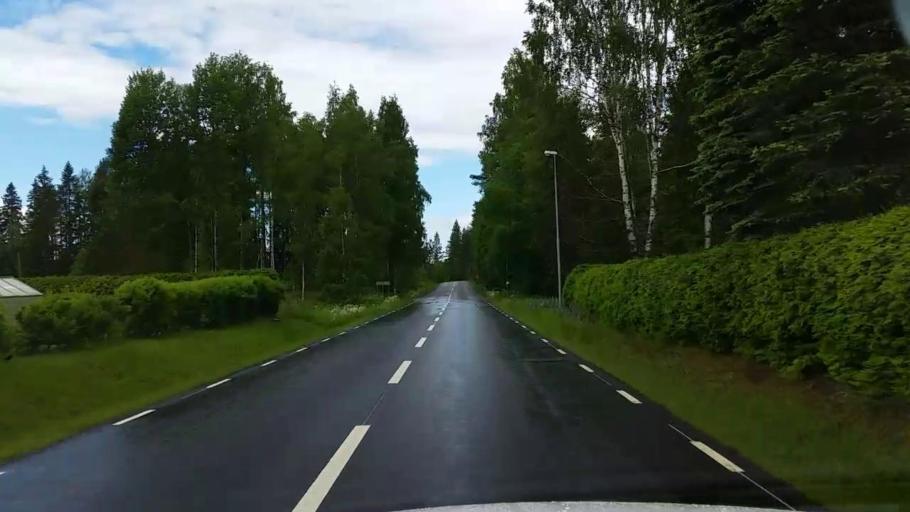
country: SE
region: Gaevleborg
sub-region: Sandvikens Kommun
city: Jarbo
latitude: 60.8451
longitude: 16.4642
